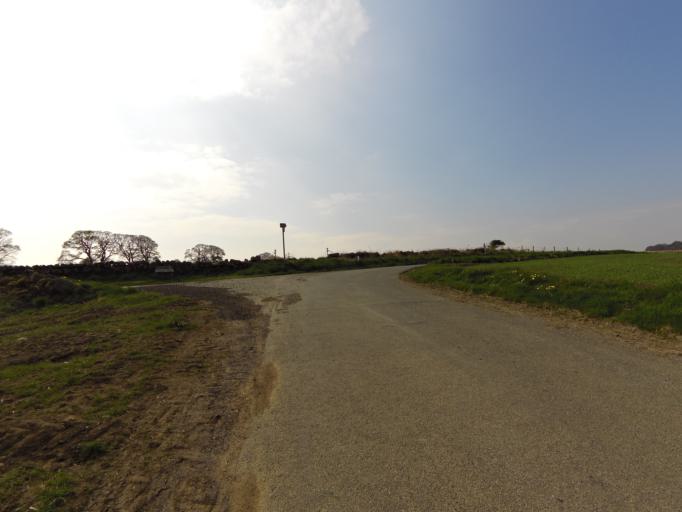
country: GB
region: Scotland
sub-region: Fife
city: Kinghorn
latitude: 56.0860
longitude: -3.1862
